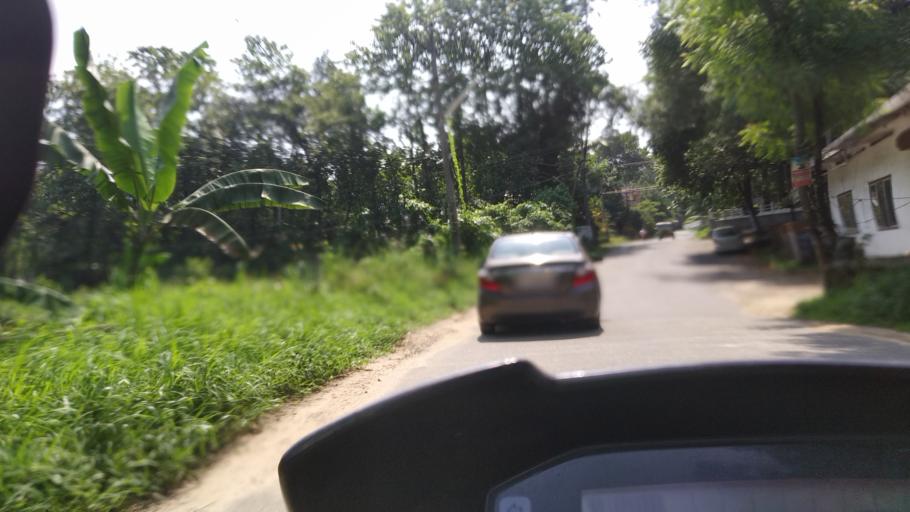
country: IN
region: Kerala
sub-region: Kottayam
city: Erattupetta
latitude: 9.6985
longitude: 76.8148
